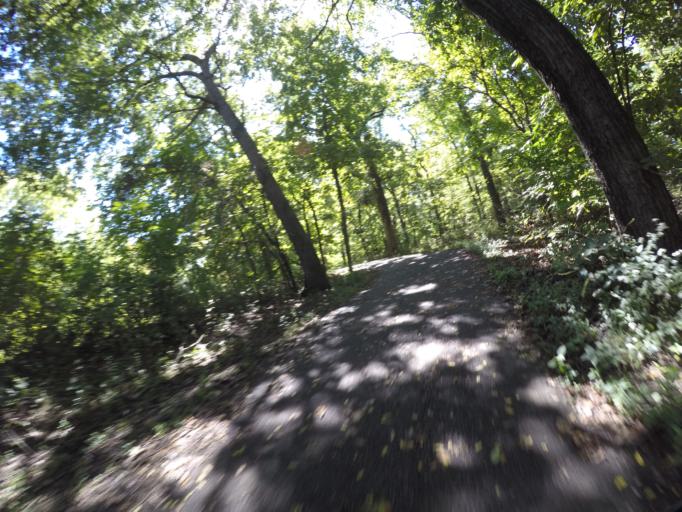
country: US
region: Kansas
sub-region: Johnson County
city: Lenexa
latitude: 38.9197
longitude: -94.7075
